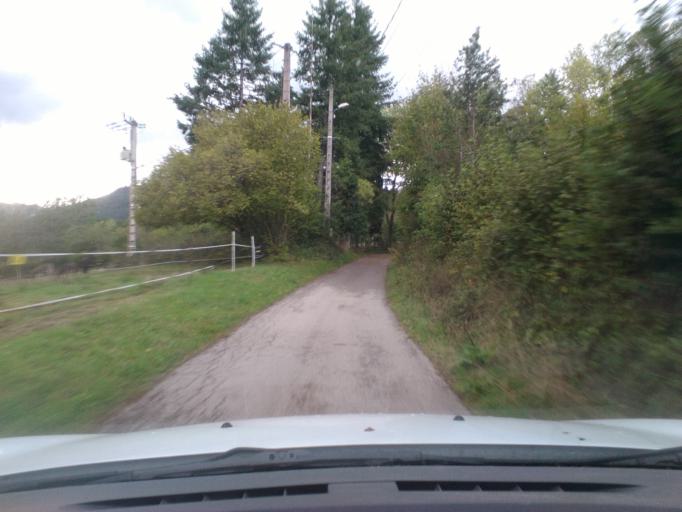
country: FR
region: Lorraine
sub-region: Departement des Vosges
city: Saint-Die-des-Vosges
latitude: 48.3187
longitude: 6.9828
